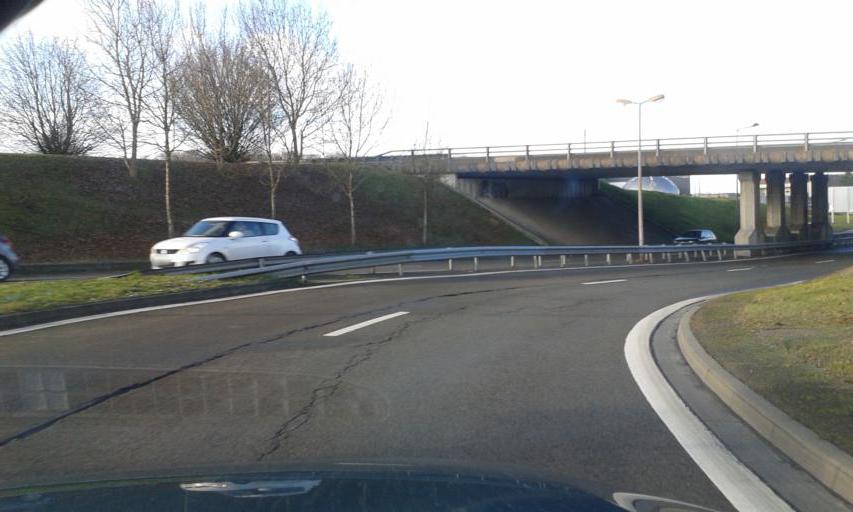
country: FR
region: Picardie
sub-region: Departement de l'Oise
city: Jaux
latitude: 49.4100
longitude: 2.7748
